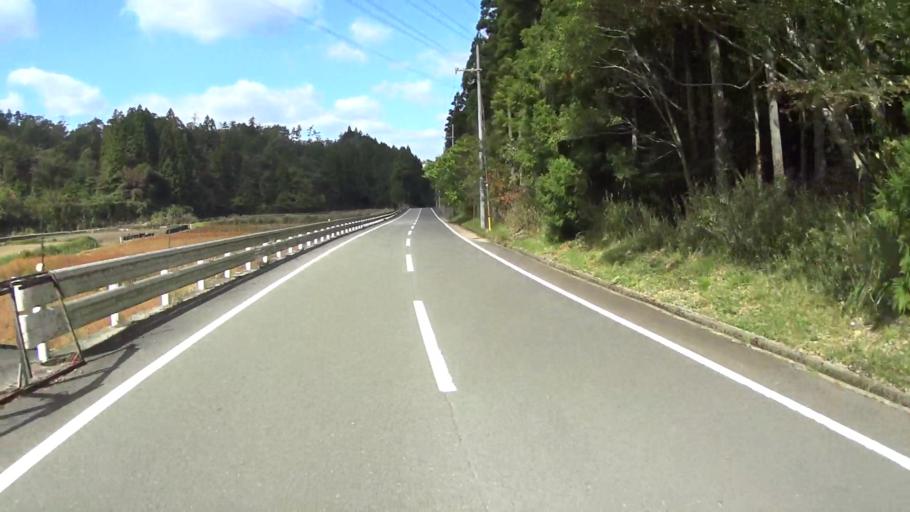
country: JP
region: Kyoto
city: Kameoka
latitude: 35.1164
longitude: 135.5666
